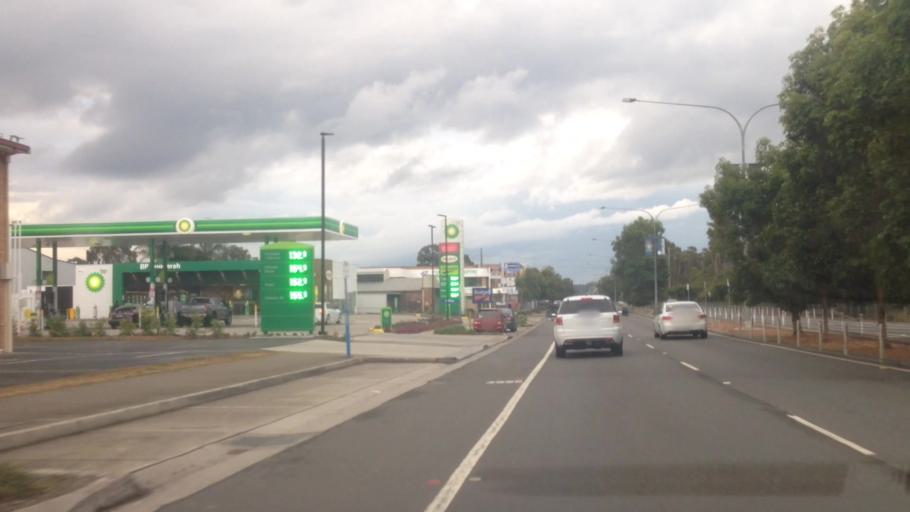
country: AU
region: New South Wales
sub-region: Wyong Shire
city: Chittaway Bay
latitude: -33.3064
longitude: 151.4200
